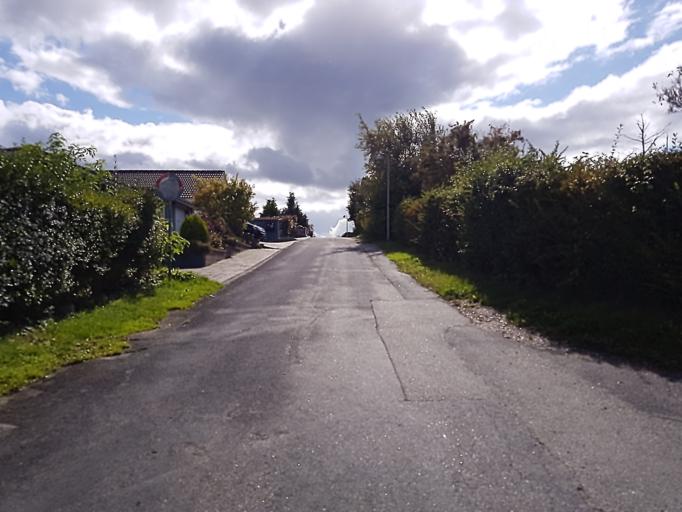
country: DK
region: Zealand
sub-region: Roskilde Kommune
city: Jyllinge
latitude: 55.7709
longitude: 12.0963
